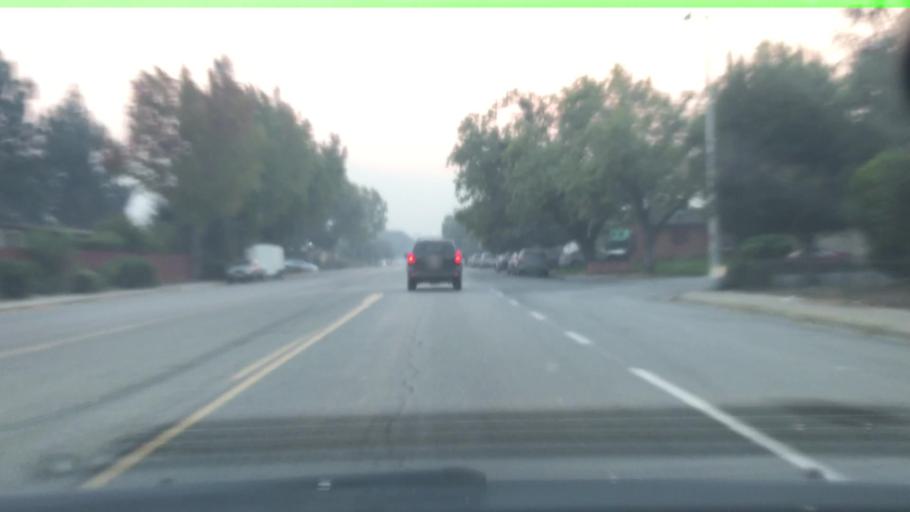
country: US
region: California
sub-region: Santa Clara County
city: Gilroy
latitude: 36.9990
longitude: -121.5702
